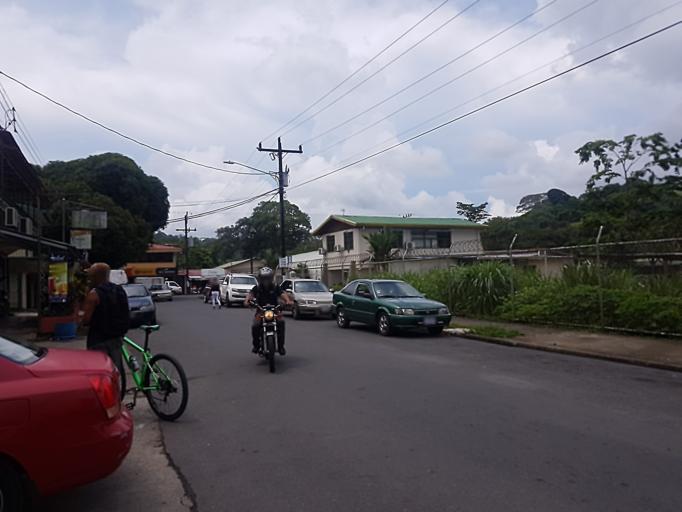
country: CR
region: Heredia
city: La Virgen
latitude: 10.4561
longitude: -84.0073
